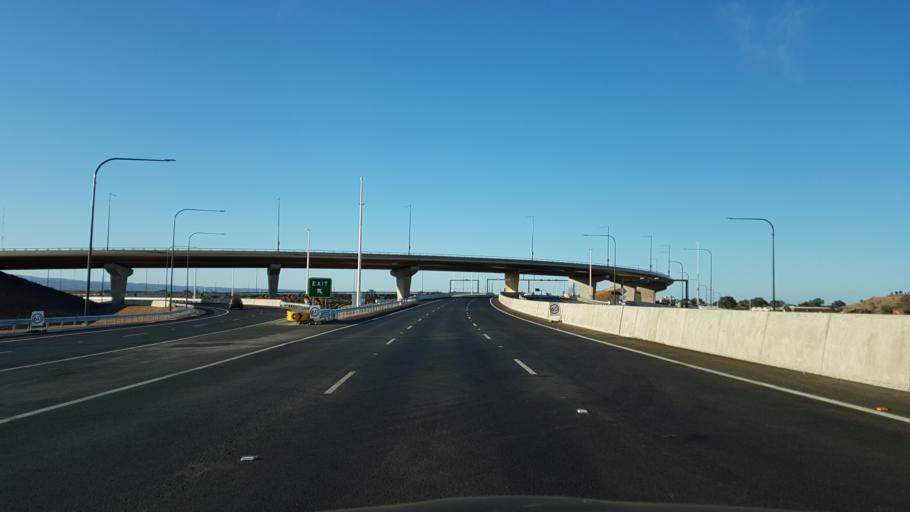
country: AU
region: South Australia
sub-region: Port Adelaide Enfield
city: Blair Athol
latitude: -34.8273
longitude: 138.5628
